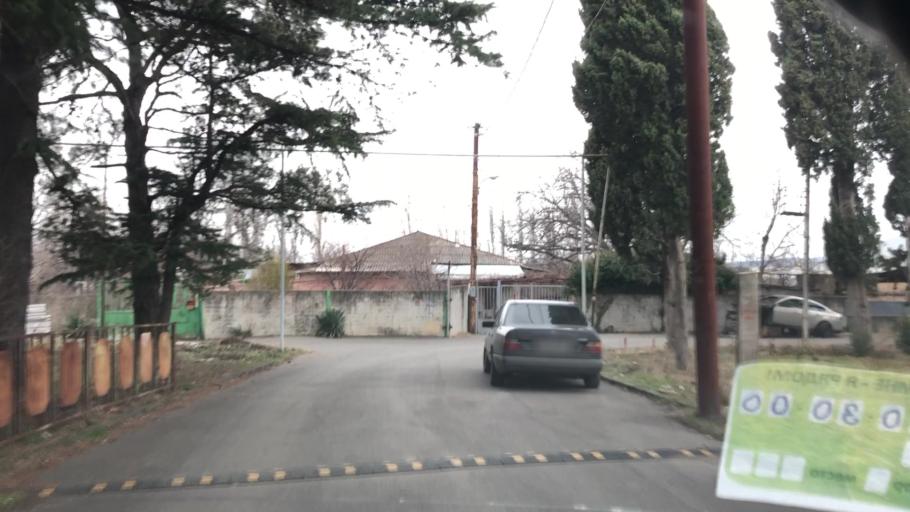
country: GE
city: Didi Lilo
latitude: 41.7022
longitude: 44.9274
